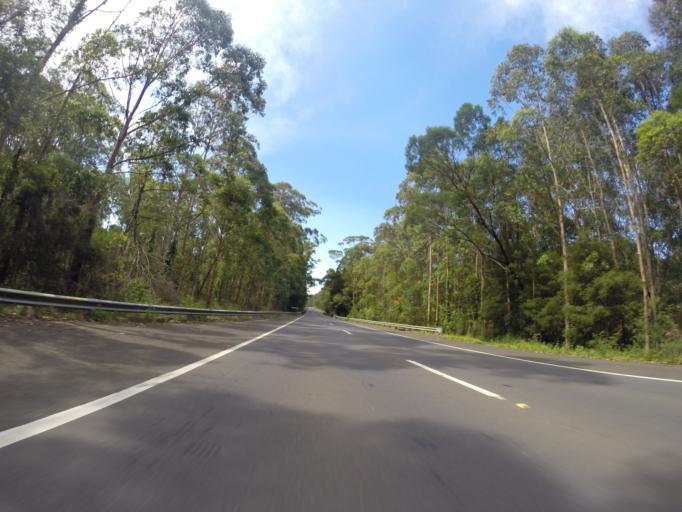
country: AU
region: New South Wales
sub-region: Shoalhaven Shire
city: Falls Creek
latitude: -35.0627
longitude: 150.5738
